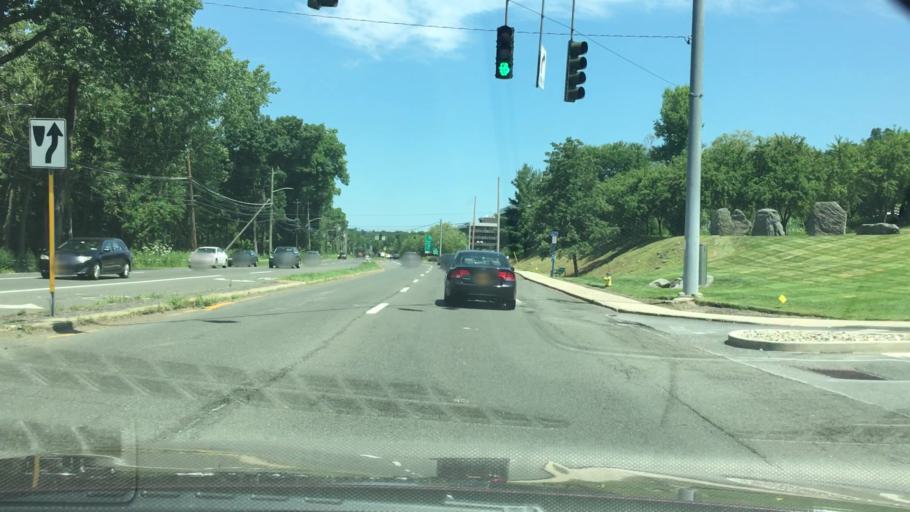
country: US
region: New York
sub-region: Westchester County
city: Mamaroneck
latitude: 40.9766
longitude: -73.7430
